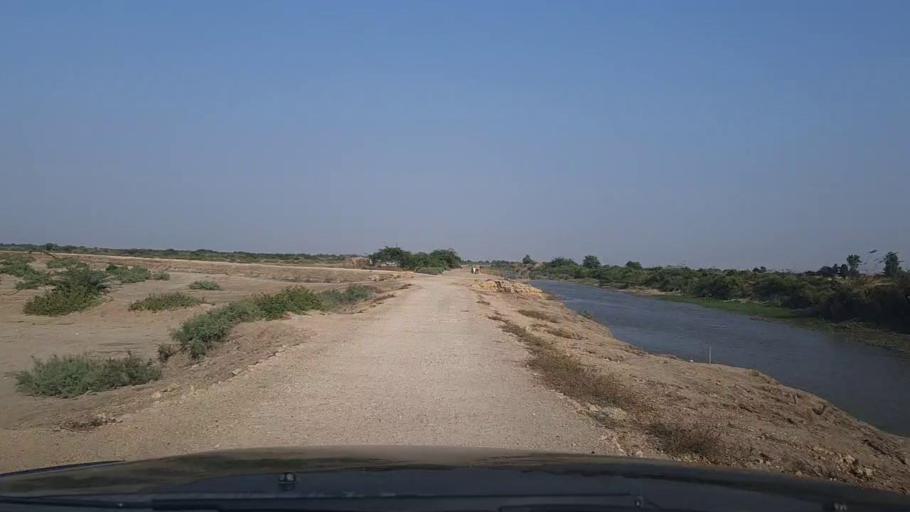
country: PK
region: Sindh
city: Mirpur Sakro
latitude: 24.6415
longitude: 67.7508
